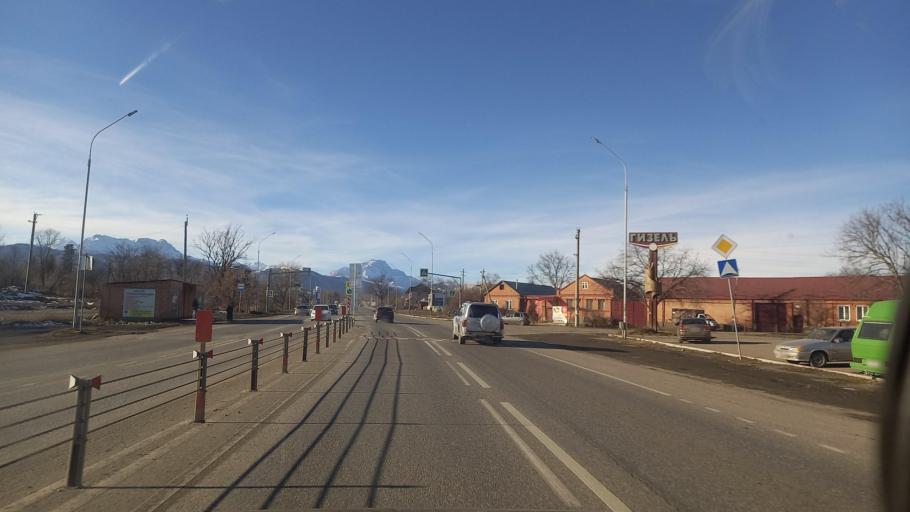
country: RU
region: North Ossetia
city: Gizel'
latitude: 43.0284
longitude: 44.5776
